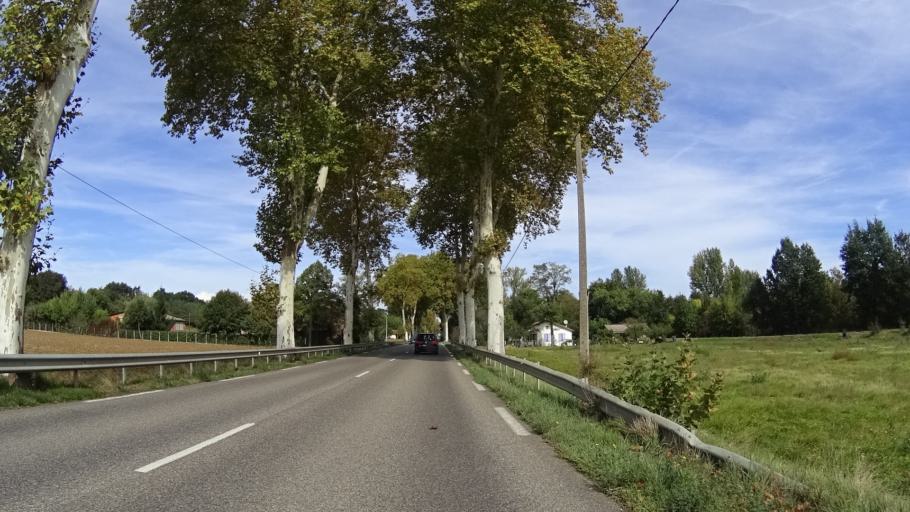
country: FR
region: Aquitaine
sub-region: Departement du Lot-et-Garonne
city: Astaffort
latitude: 44.0908
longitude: 0.6541
